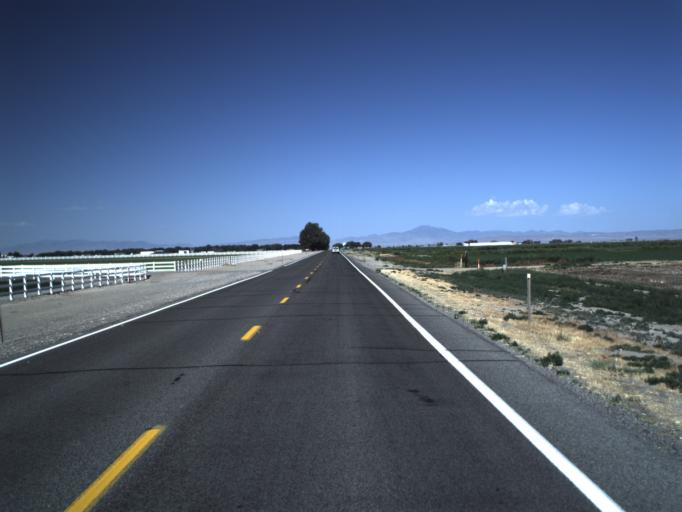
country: US
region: Utah
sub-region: Millard County
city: Delta
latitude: 39.3306
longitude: -112.6324
